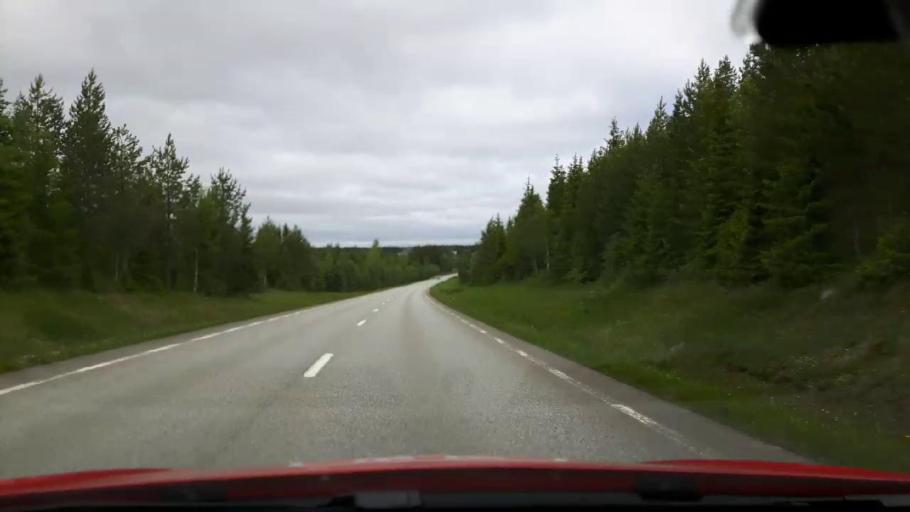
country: SE
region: Jaemtland
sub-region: Krokoms Kommun
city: Krokom
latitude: 63.5075
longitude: 14.5173
